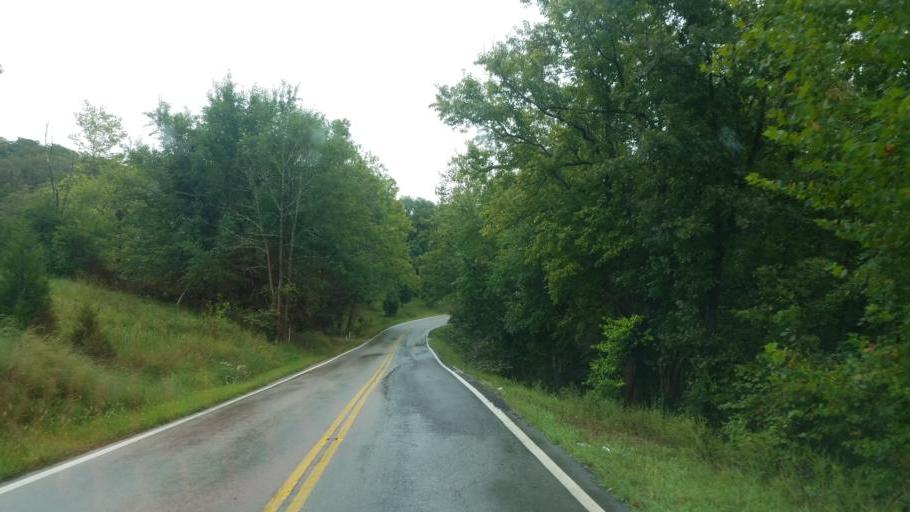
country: US
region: Ohio
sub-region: Adams County
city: West Union
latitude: 38.7866
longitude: -83.5399
